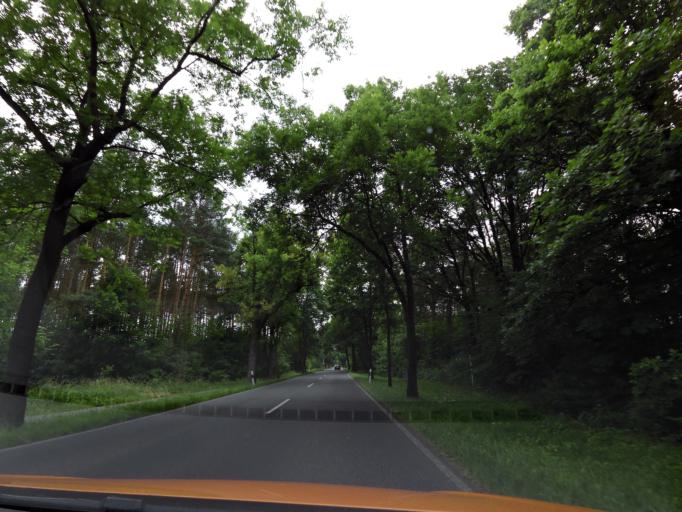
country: DE
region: Brandenburg
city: Zossen
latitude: 52.1876
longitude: 13.4634
